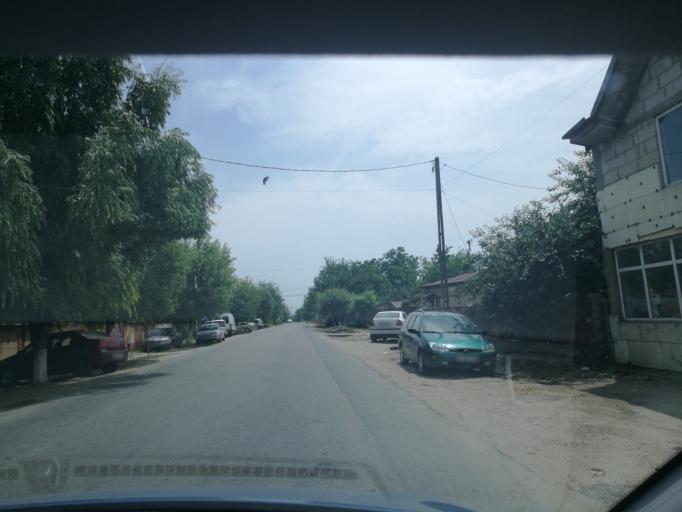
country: RO
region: Ilfov
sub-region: Comuna Jilava
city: Jilava
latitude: 44.3266
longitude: 26.0909
